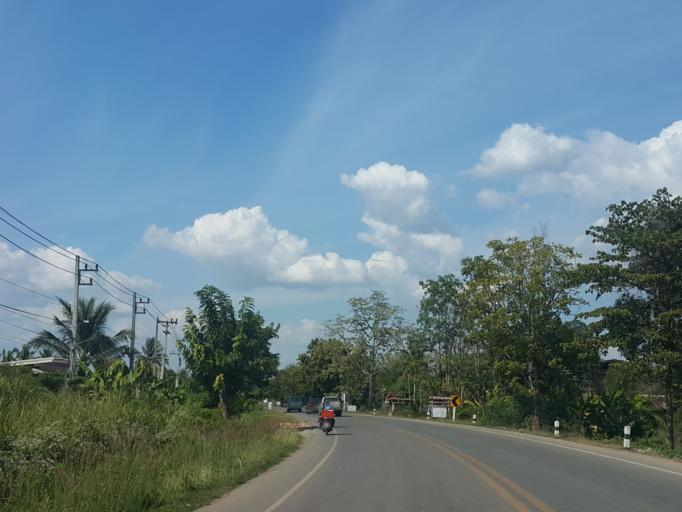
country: TH
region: Sukhothai
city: Sawankhalok
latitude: 17.2867
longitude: 99.8345
